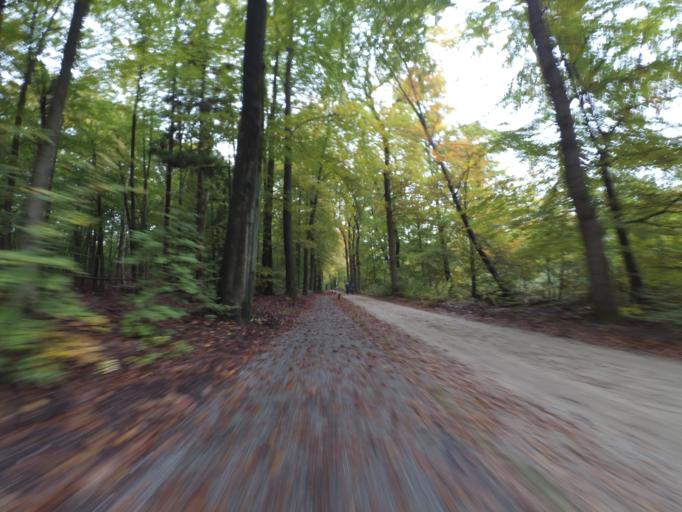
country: NL
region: Gelderland
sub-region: Gemeente Barneveld
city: Garderen
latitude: 52.3076
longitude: 5.7135
